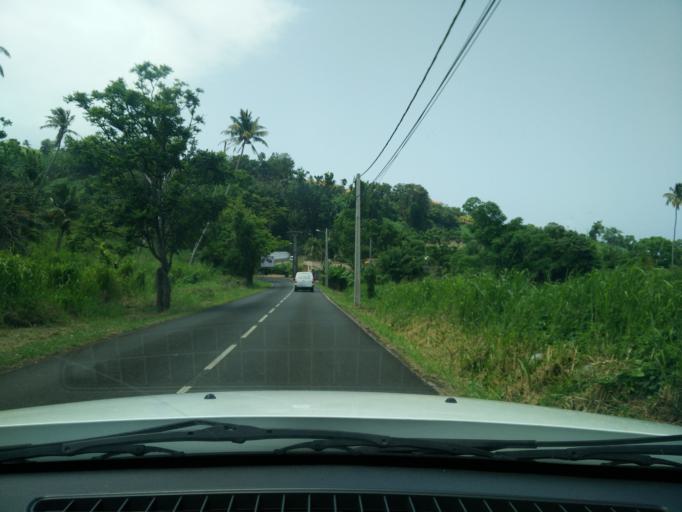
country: GP
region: Guadeloupe
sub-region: Guadeloupe
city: Trois-Rivieres
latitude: 15.9768
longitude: -61.6360
